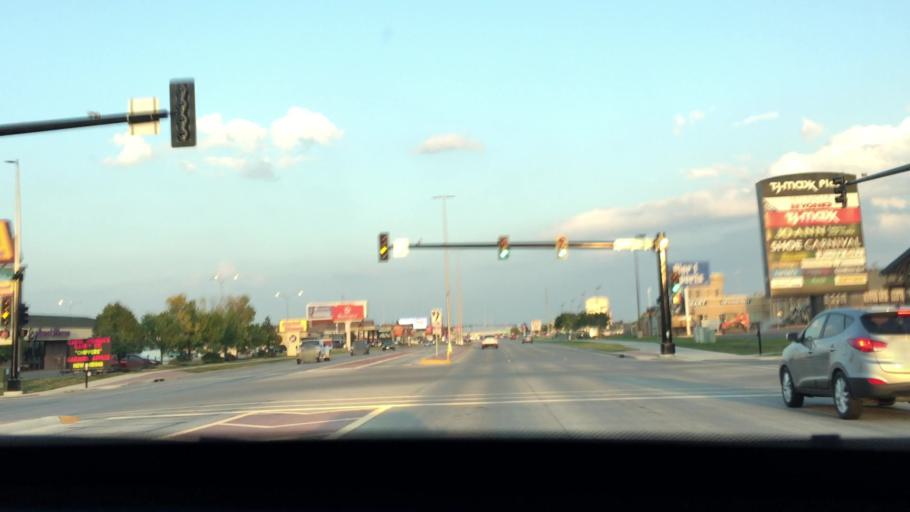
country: US
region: North Dakota
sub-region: Cass County
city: West Fargo
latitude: 46.8618
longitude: -96.8572
